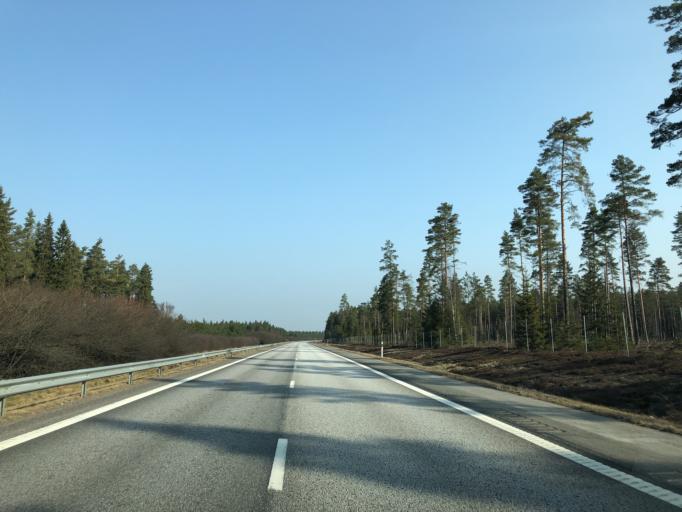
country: SE
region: Joenkoeping
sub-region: Varnamo Kommun
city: Varnamo
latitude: 57.2705
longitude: 14.0828
